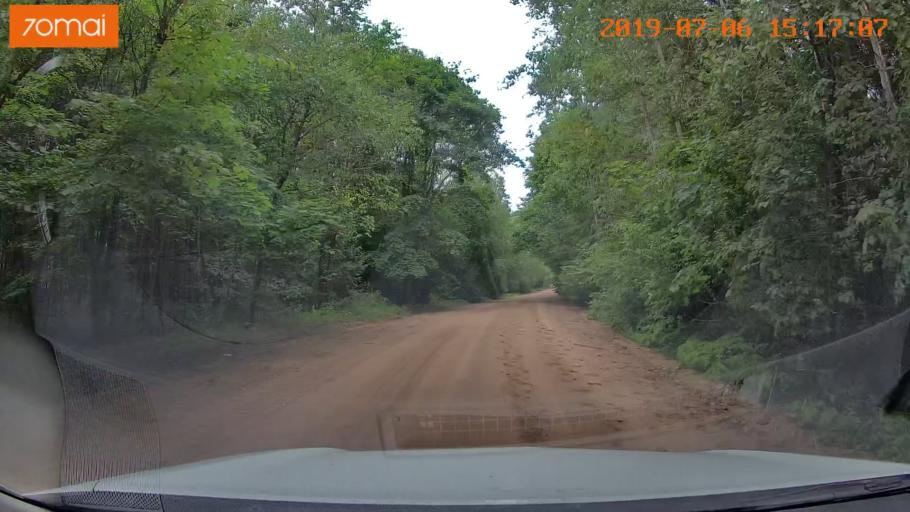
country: BY
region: Minsk
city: Ivyanyets
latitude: 53.9859
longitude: 26.6697
